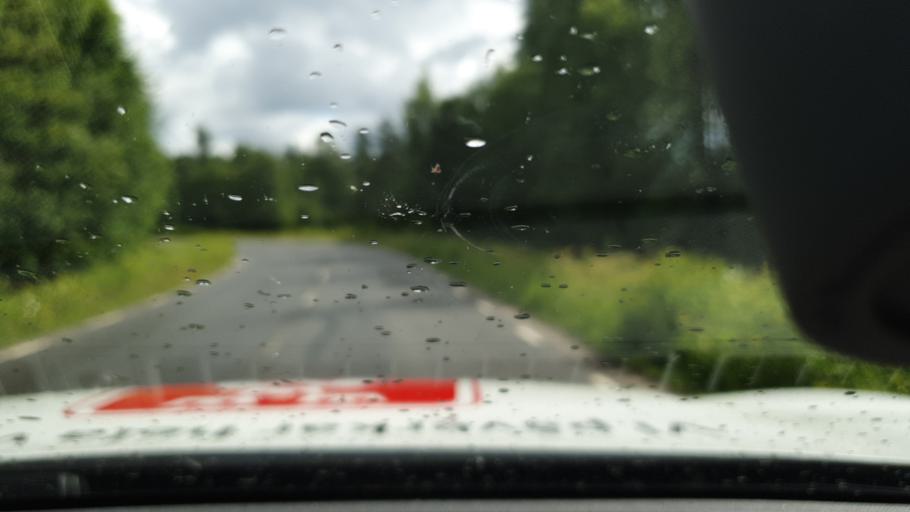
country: SE
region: Norrbotten
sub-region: Bodens Kommun
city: Boden
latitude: 65.8477
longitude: 21.7235
